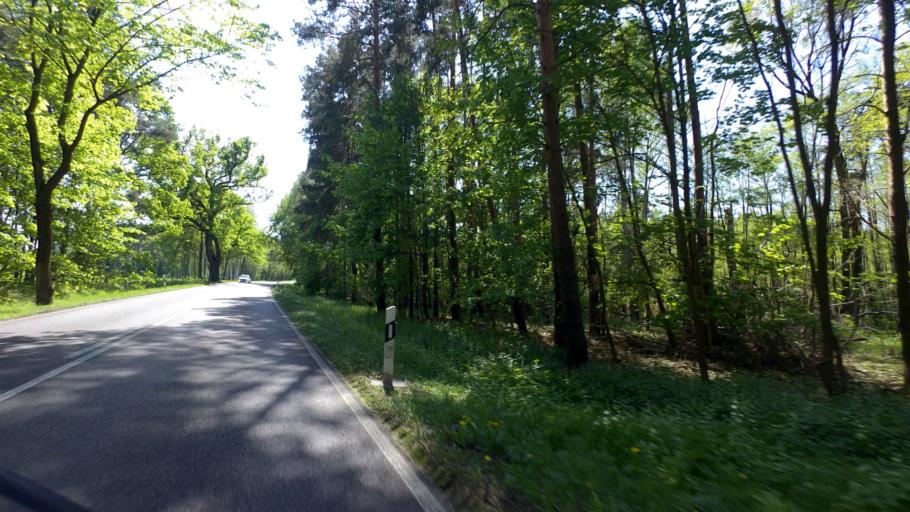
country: DE
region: Brandenburg
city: Tauche
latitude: 52.1398
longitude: 14.2061
